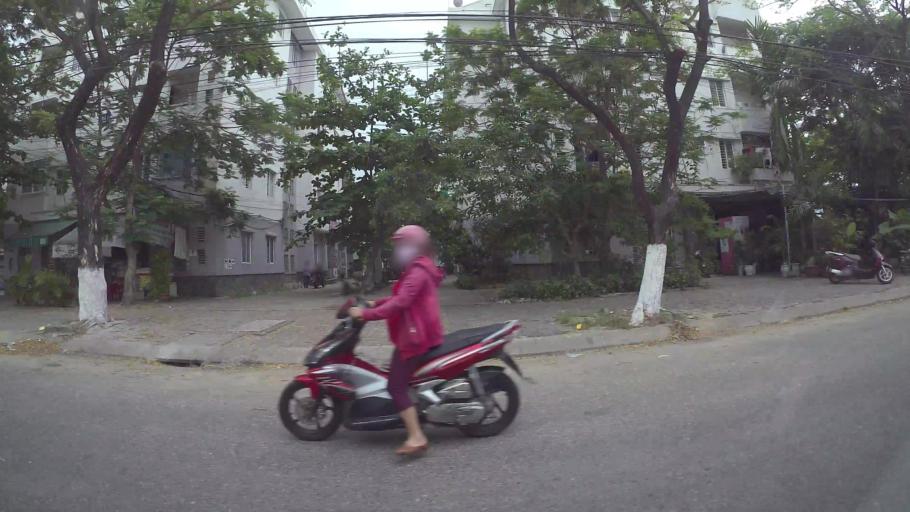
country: VN
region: Da Nang
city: Lien Chieu
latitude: 16.0748
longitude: 108.1677
